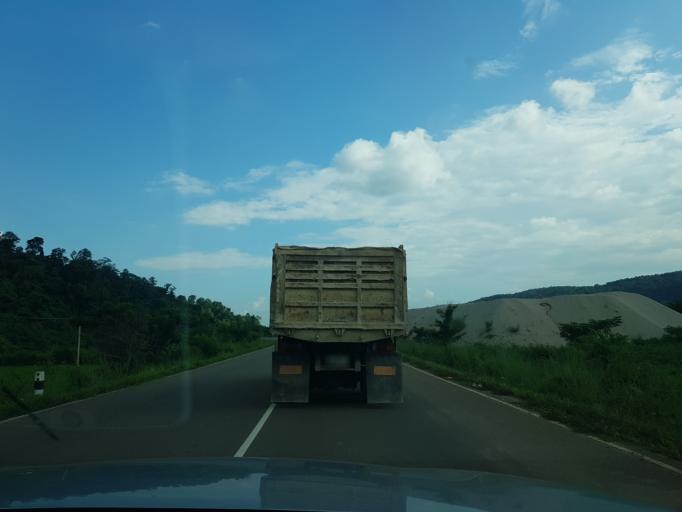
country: TH
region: Nong Khai
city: Pho Tak
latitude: 18.0112
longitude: 102.4013
